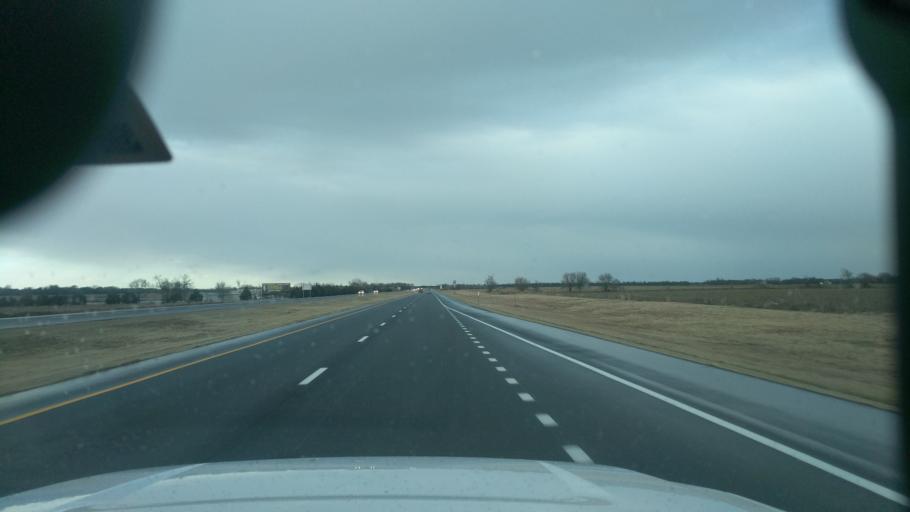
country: US
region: Kansas
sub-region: Harvey County
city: Newton
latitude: 37.9601
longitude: -97.3274
